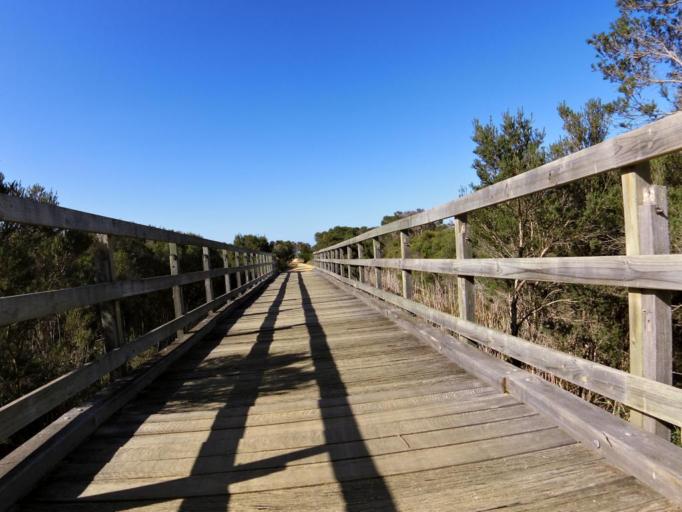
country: AU
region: Victoria
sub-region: Bass Coast
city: North Wonthaggi
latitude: -38.5799
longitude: 145.5522
